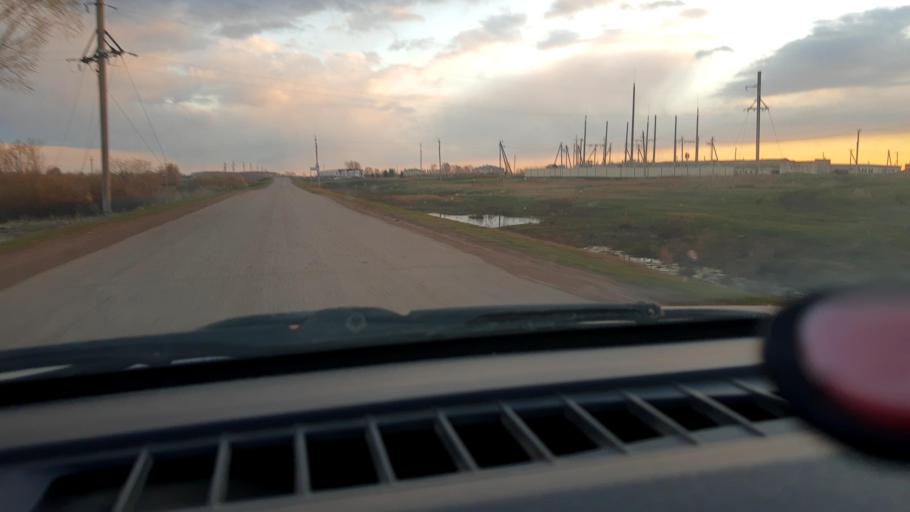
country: RU
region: Bashkortostan
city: Asanovo
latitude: 54.9117
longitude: 55.5010
